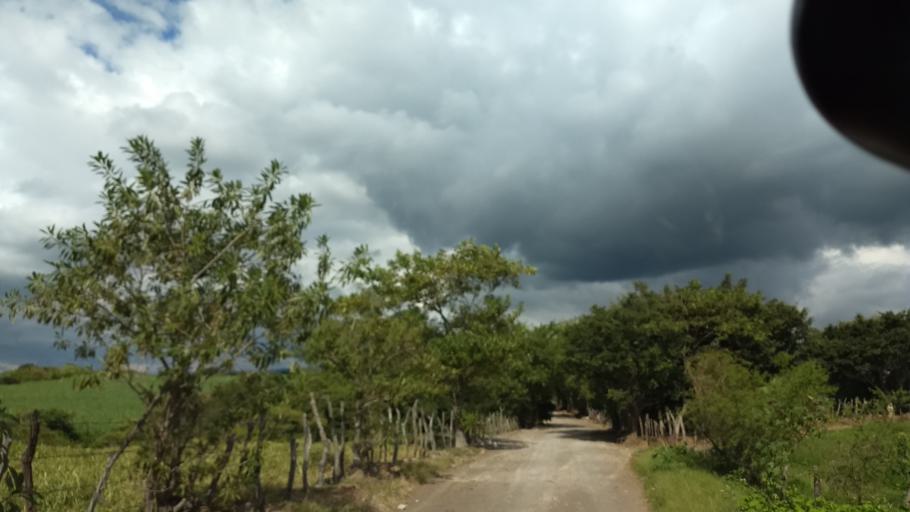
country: MX
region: Colima
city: Suchitlan
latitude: 19.4573
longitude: -103.7672
